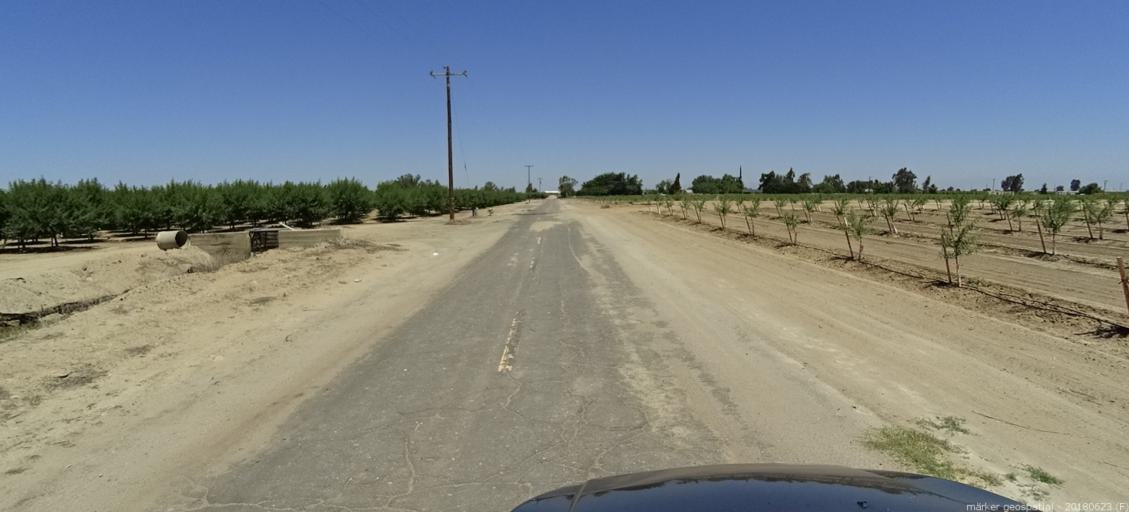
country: US
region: California
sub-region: Madera County
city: Chowchilla
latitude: 37.0960
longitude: -120.2385
